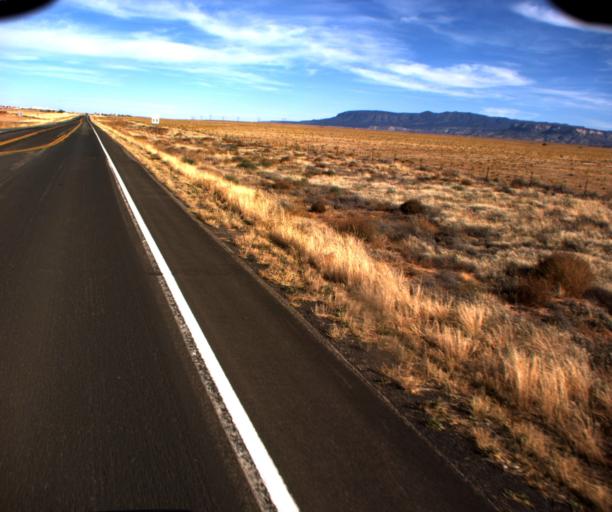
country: US
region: Arizona
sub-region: Apache County
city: Lukachukai
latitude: 36.9608
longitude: -109.3837
